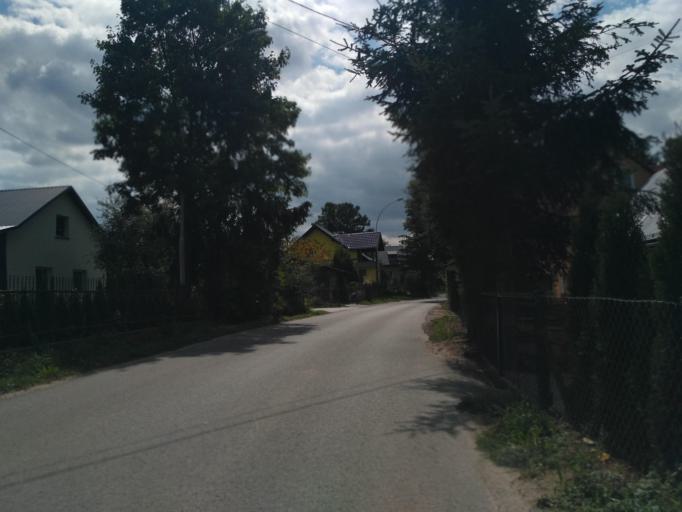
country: PL
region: Subcarpathian Voivodeship
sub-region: Powiat rzeszowski
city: Dynow
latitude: 49.8083
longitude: 22.2516
